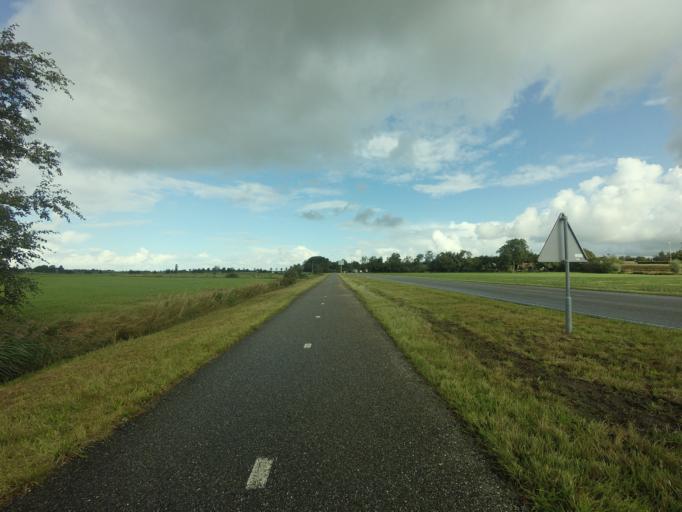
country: NL
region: Friesland
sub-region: Gemeente Tytsjerksteradiel
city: Garyp
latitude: 53.1584
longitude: 5.9504
